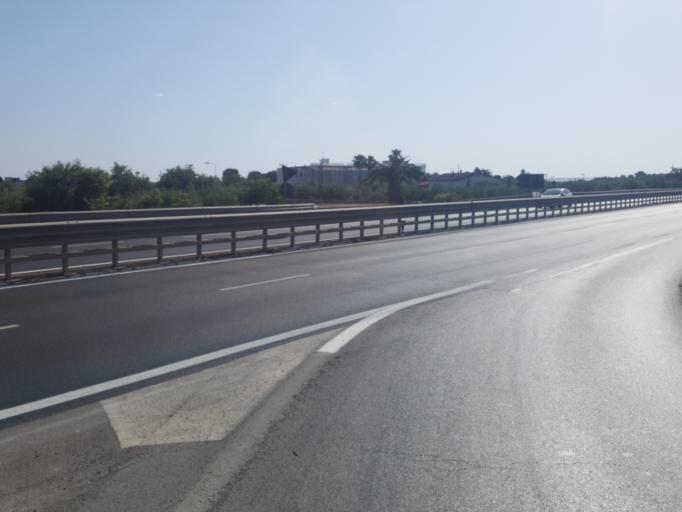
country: IT
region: Apulia
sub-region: Provincia di Barletta - Andria - Trani
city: Barletta
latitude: 41.3023
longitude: 16.3109
